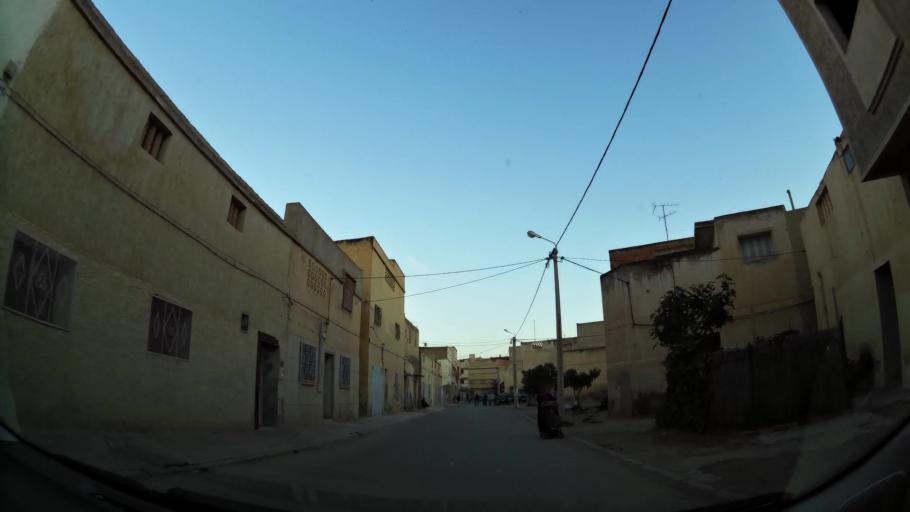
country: MA
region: Oriental
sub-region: Oujda-Angad
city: Oujda
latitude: 34.6980
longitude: -1.9215
